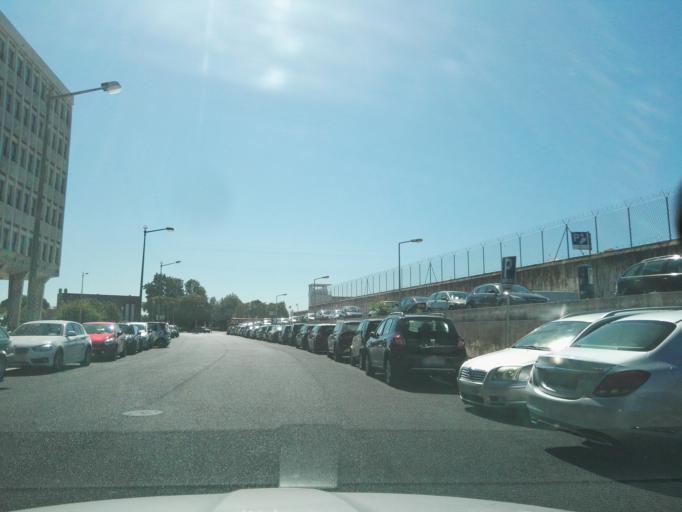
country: PT
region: Lisbon
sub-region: Lisbon
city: Lisbon
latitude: 38.7320
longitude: -9.1578
